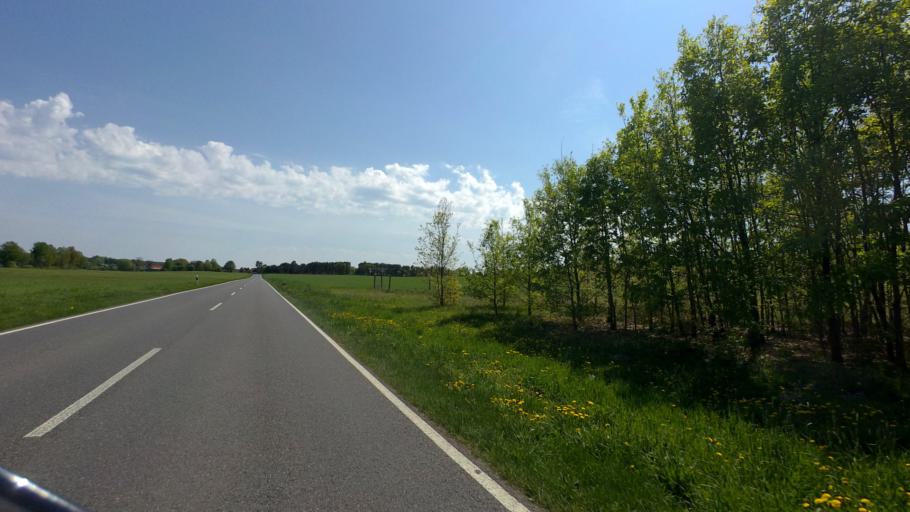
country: DE
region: Brandenburg
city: Lieberose
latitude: 51.9876
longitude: 14.2111
